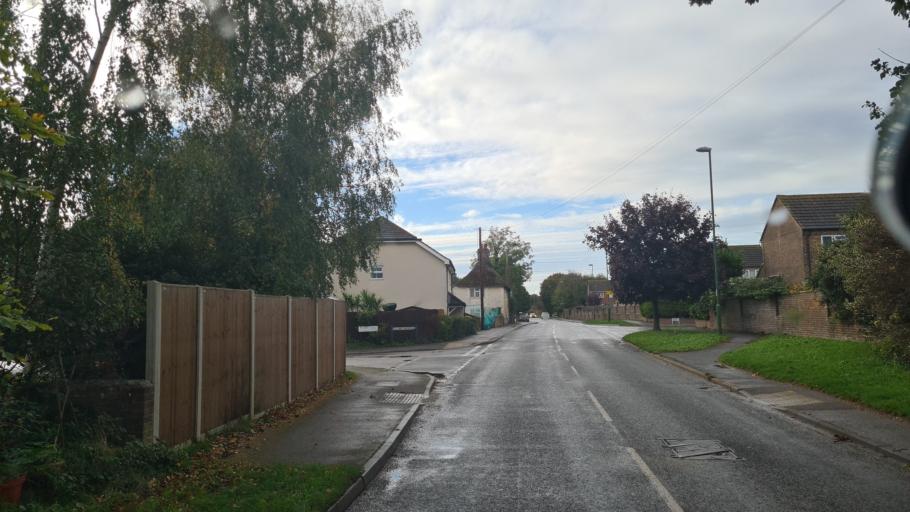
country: GB
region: England
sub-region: West Sussex
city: Walberton
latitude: 50.8180
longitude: -0.6044
